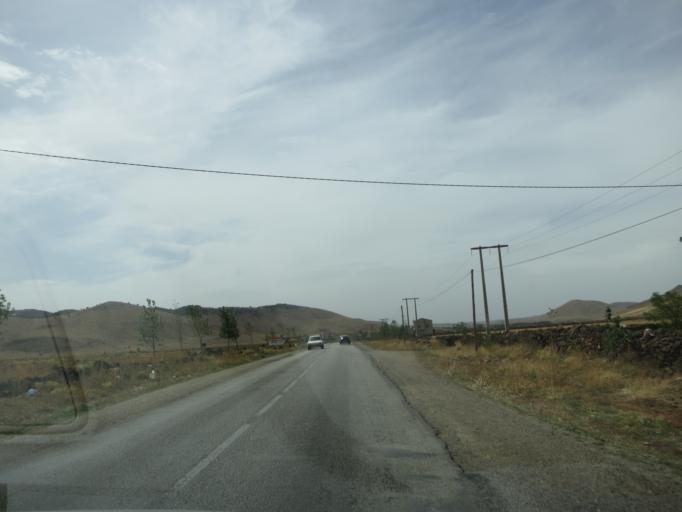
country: MA
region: Meknes-Tafilalet
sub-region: Ifrane
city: Azrou
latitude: 33.2267
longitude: -5.0601
